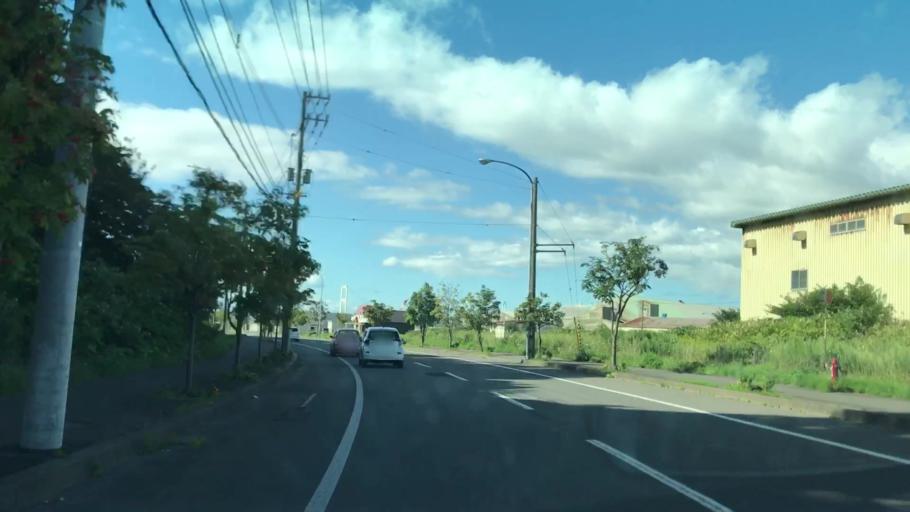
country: JP
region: Hokkaido
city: Muroran
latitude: 42.3293
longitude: 140.9672
